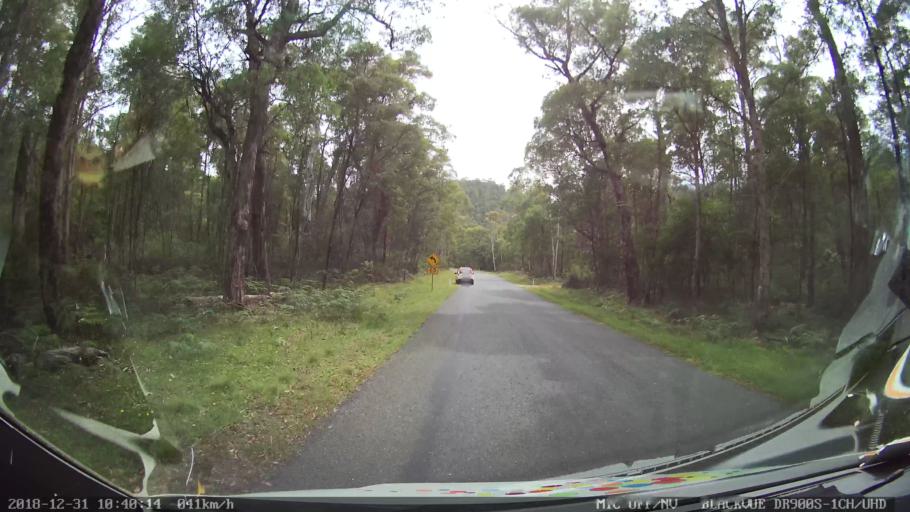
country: AU
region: New South Wales
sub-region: Snowy River
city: Jindabyne
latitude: -36.3923
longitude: 148.1804
